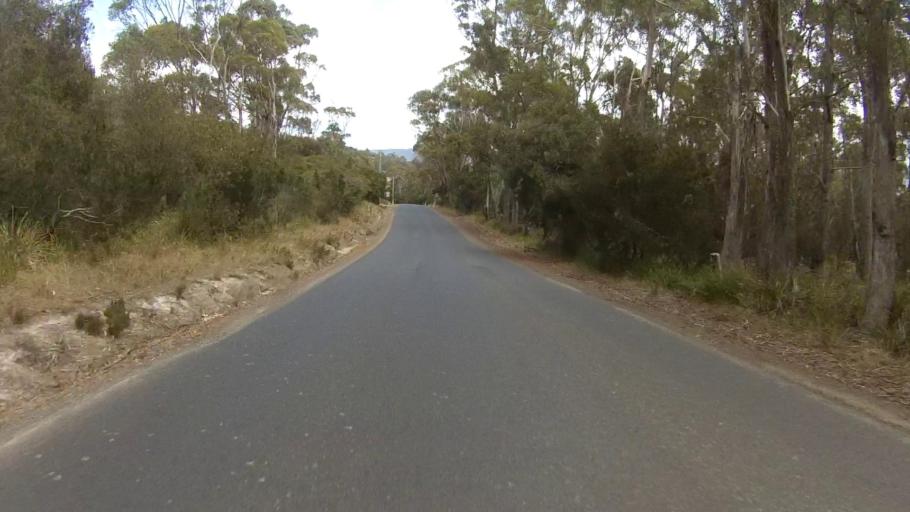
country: AU
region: Tasmania
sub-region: Kingborough
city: Blackmans Bay
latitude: -43.0280
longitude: 147.3126
